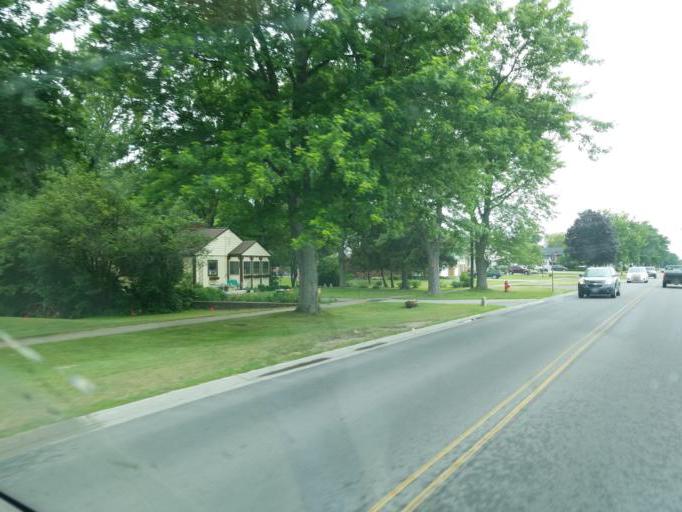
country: US
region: New York
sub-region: Erie County
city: Tonawanda
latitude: 43.0127
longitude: -78.9001
